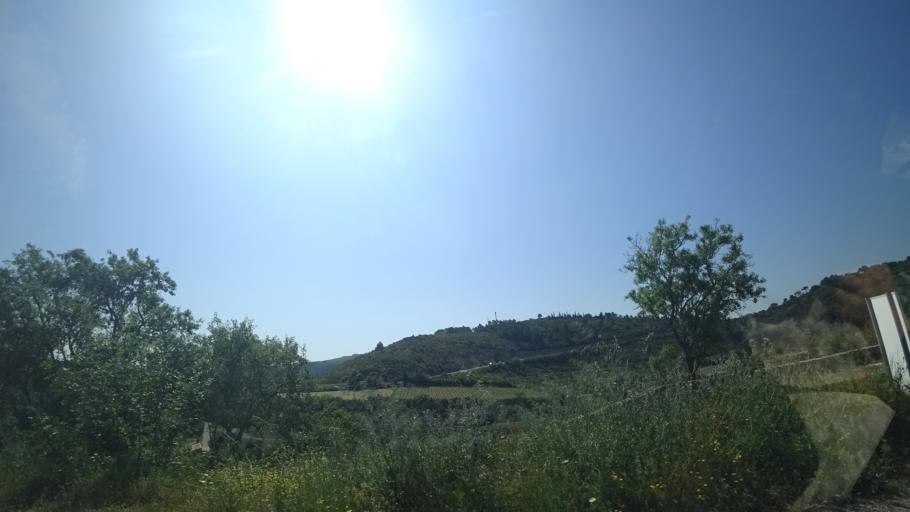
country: FR
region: Languedoc-Roussillon
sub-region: Departement de l'Herault
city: Olonzac
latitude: 43.3544
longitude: 2.7404
